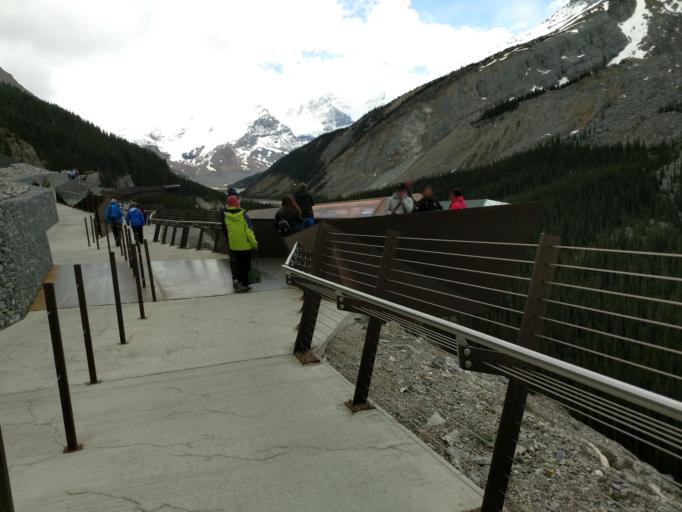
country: CA
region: Alberta
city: Jasper Park Lodge
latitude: 52.2605
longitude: -117.2796
